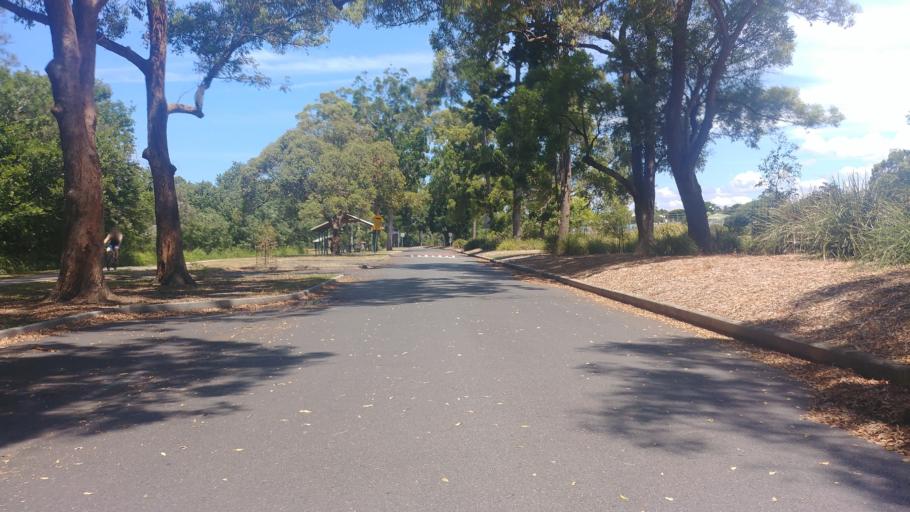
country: AU
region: Queensland
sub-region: Brisbane
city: Wavell Heights
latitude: -27.4078
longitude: 153.0539
